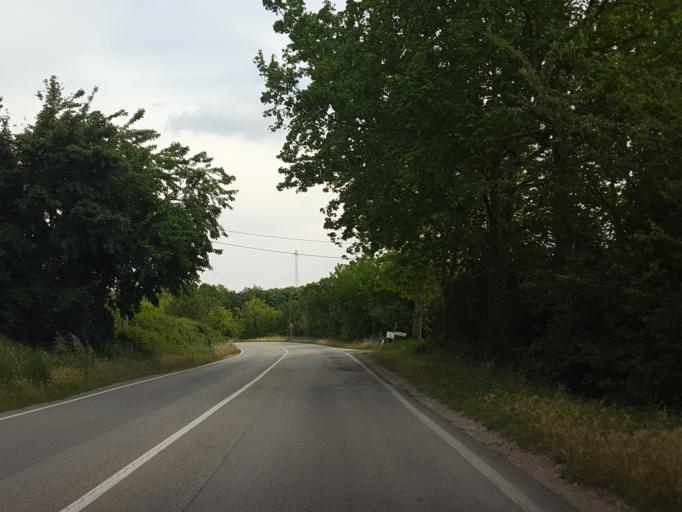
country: IT
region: Veneto
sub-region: Provincia di Vicenza
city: Alonte
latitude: 45.3532
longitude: 11.4436
